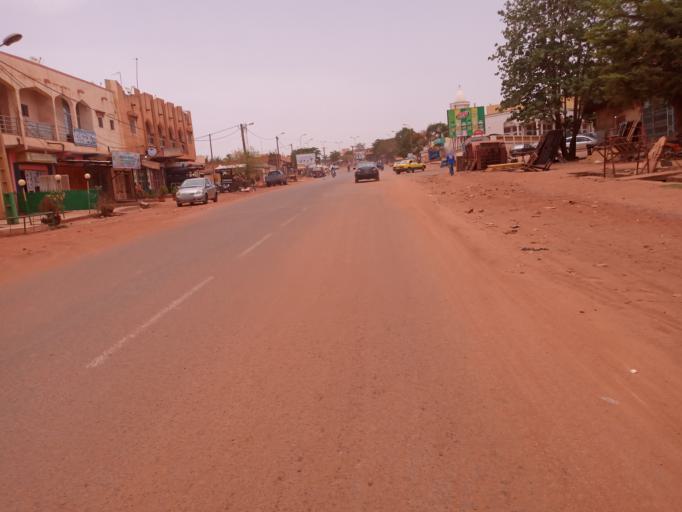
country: ML
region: Bamako
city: Bamako
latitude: 12.5745
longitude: -8.0083
